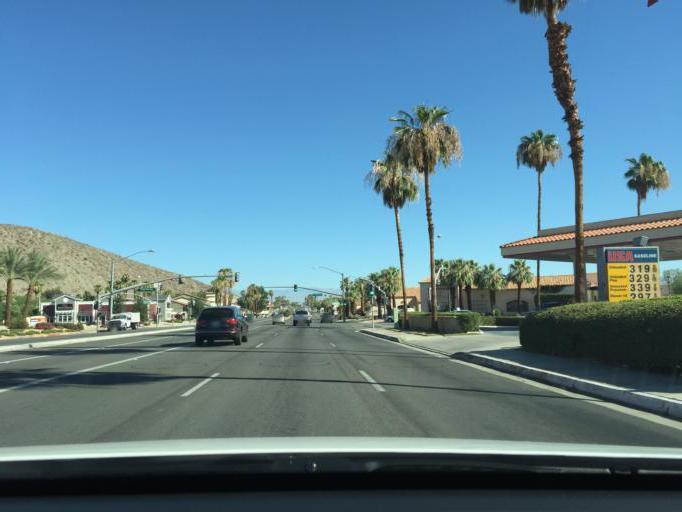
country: US
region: California
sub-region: Riverside County
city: Rancho Mirage
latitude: 33.7280
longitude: -116.4023
